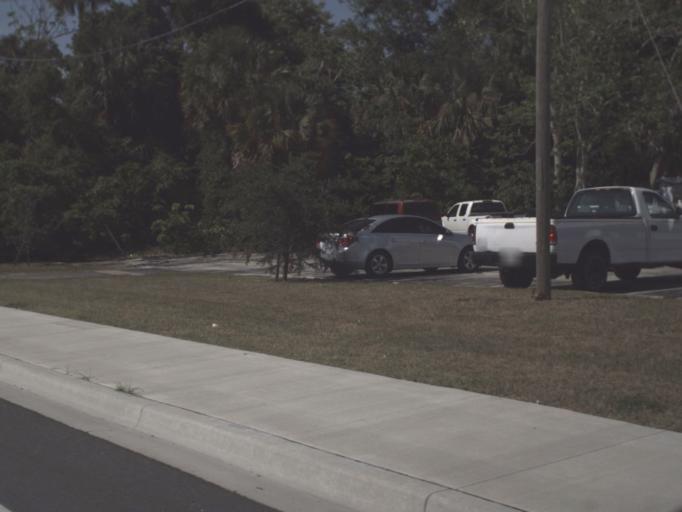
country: US
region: Florida
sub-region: Brevard County
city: Rockledge
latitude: 28.3626
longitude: -80.7342
